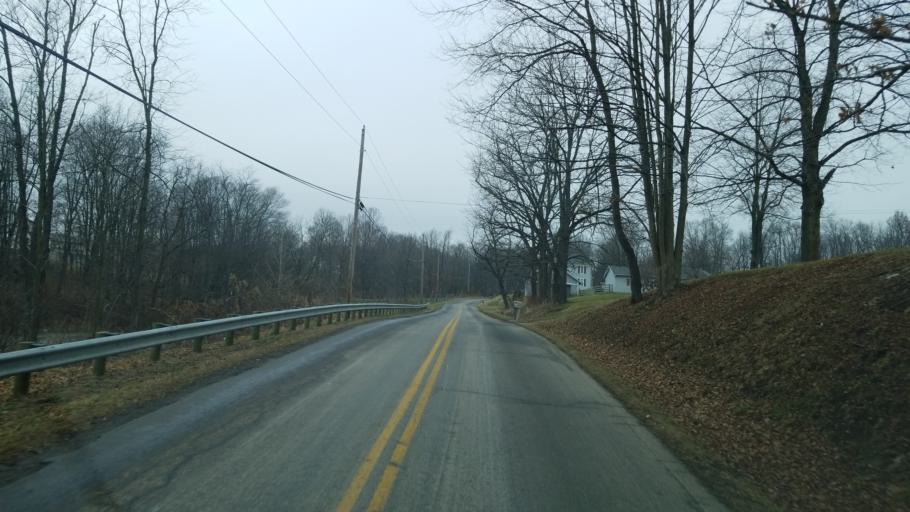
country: US
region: Ohio
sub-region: Holmes County
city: Millersburg
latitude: 40.4867
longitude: -81.8696
